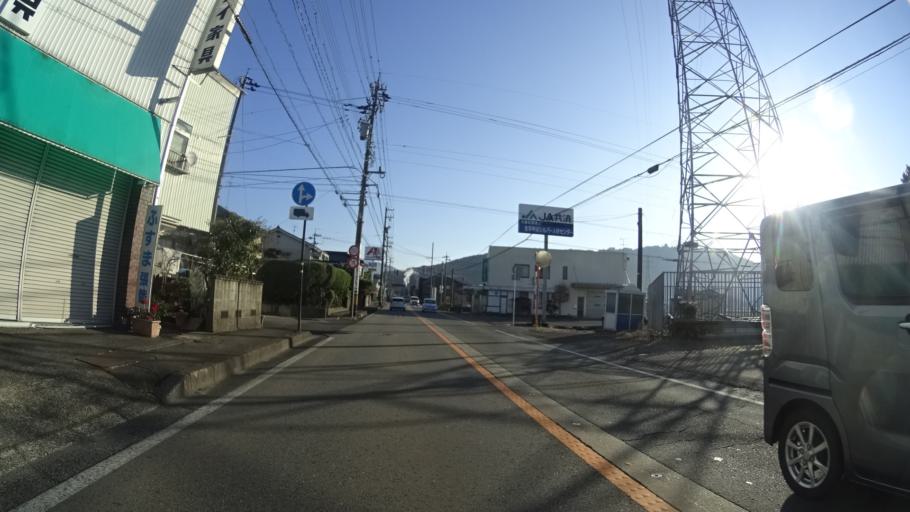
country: JP
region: Fukui
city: Maruoka
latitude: 36.0898
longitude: 136.2895
